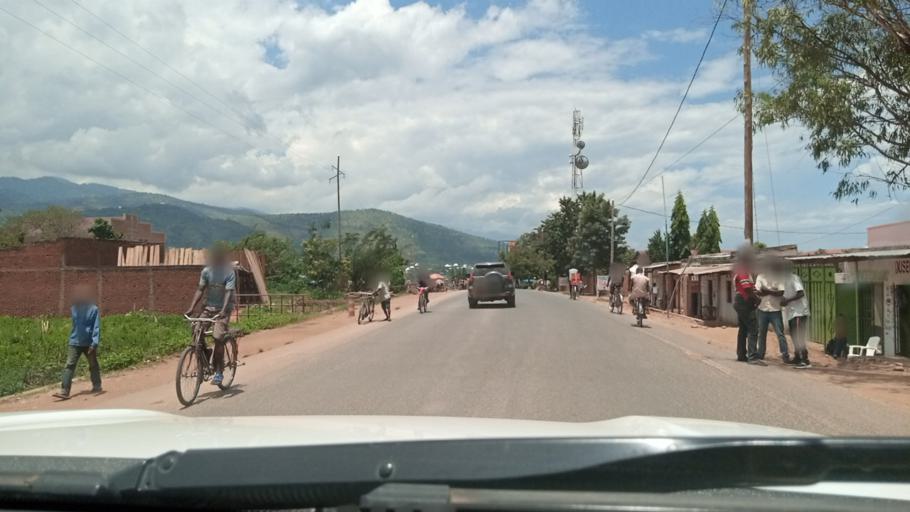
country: BI
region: Bujumbura Mairie
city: Bujumbura
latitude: -3.4704
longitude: 29.3498
